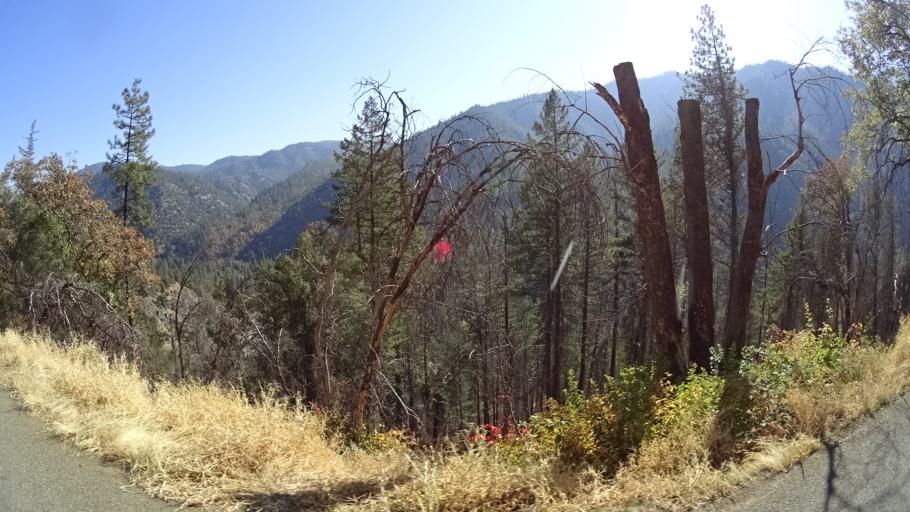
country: US
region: California
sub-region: Siskiyou County
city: Happy Camp
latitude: 41.7083
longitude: -123.0319
